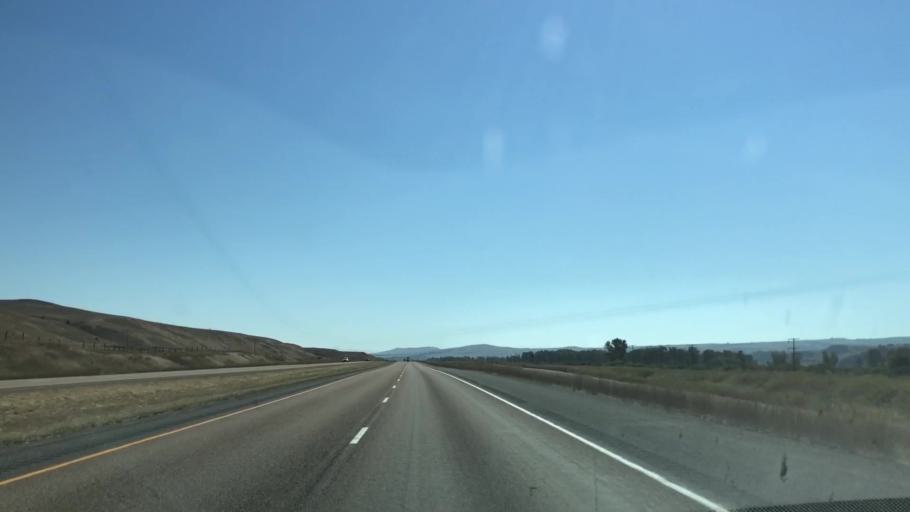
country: US
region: Montana
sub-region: Granite County
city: Philipsburg
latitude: 46.6318
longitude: -113.0869
